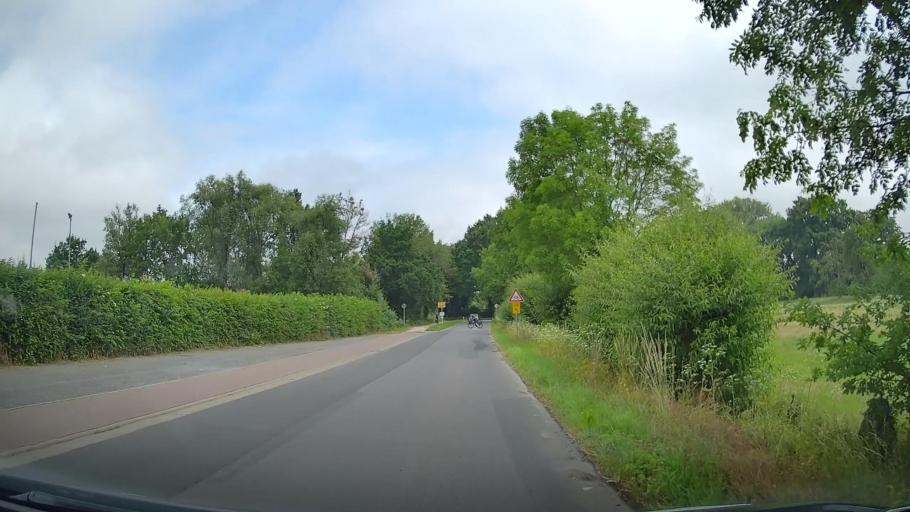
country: DE
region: Lower Saxony
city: Rinteln
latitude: 52.1686
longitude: 9.0323
